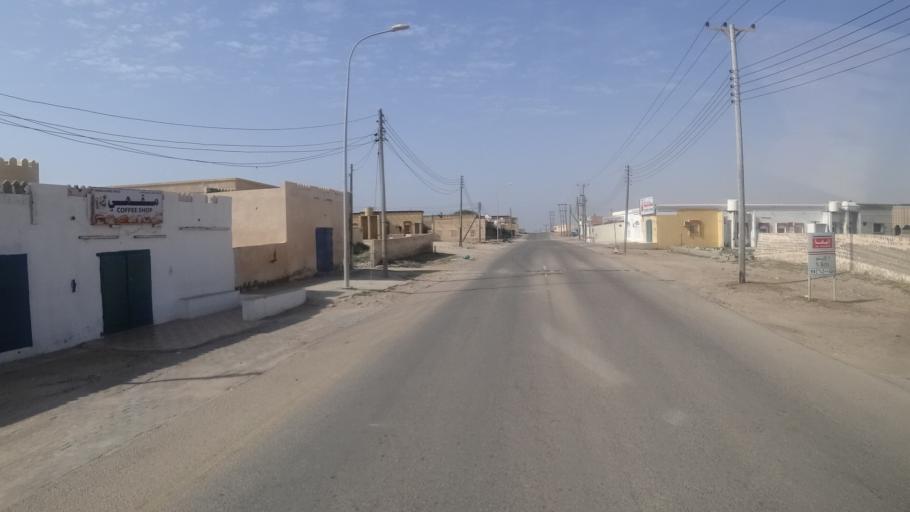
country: OM
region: Ash Sharqiyah
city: Sur
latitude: 22.1857
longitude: 59.7648
